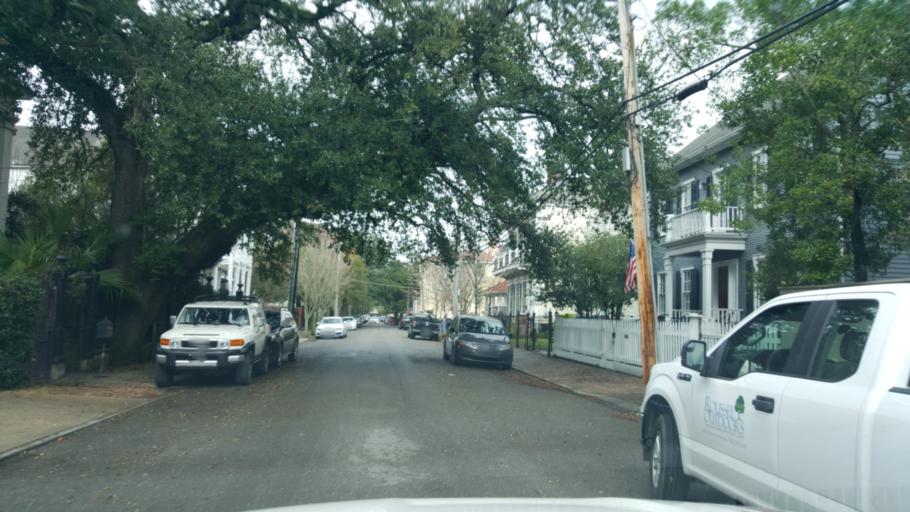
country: US
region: Louisiana
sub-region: Orleans Parish
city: New Orleans
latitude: 29.9356
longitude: -90.0746
